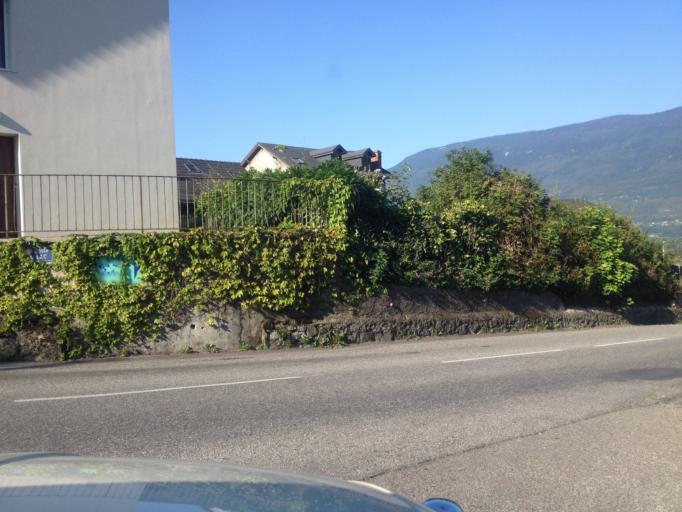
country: FR
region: Rhone-Alpes
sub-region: Departement de la Savoie
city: Viviers-du-Lac
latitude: 45.6489
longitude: 5.9051
